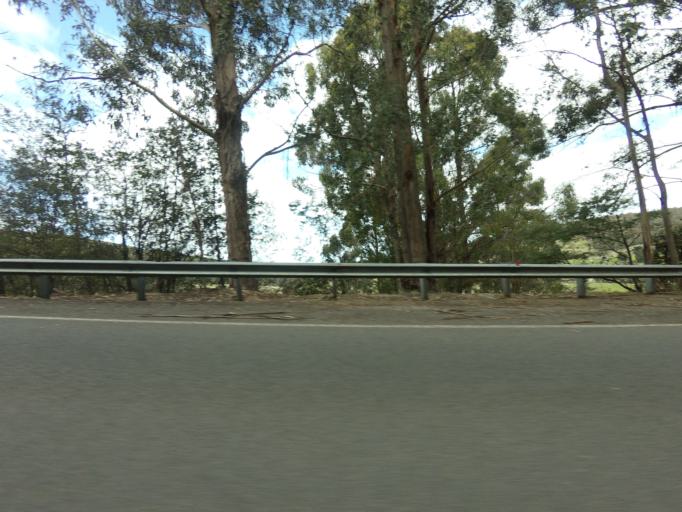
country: AU
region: Tasmania
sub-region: Huon Valley
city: Geeveston
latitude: -43.4100
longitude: 146.9578
